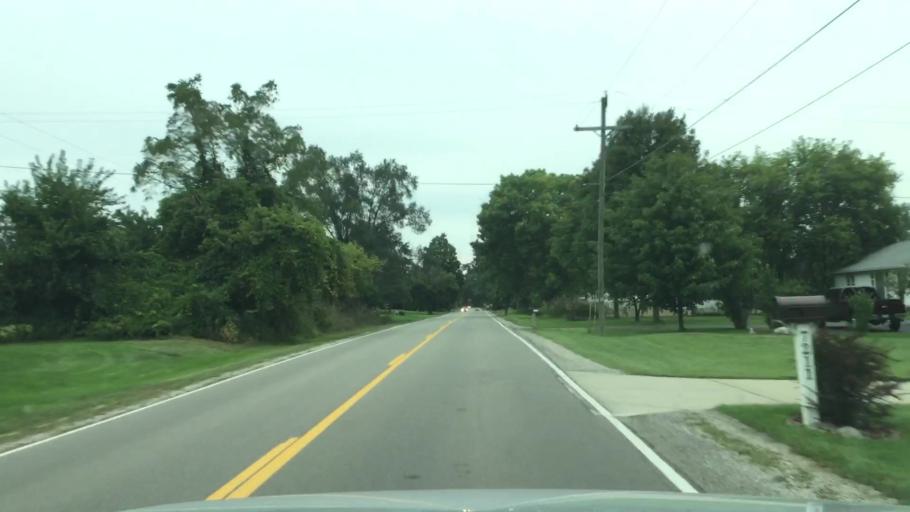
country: US
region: Michigan
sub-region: Washtenaw County
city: Ypsilanti
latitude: 42.1843
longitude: -83.6373
